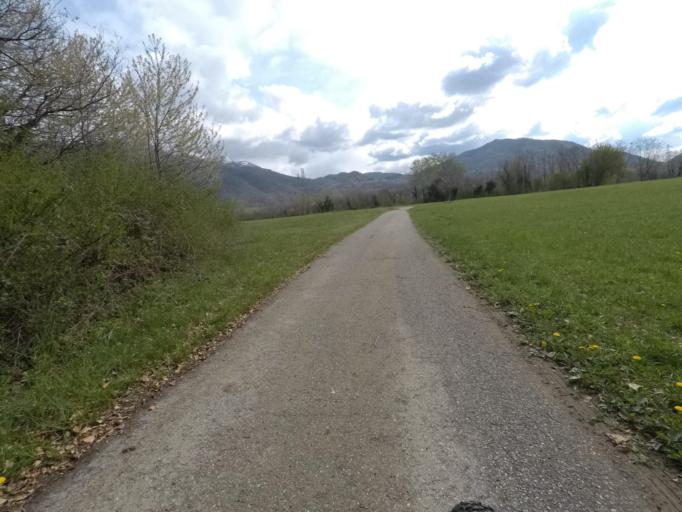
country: IT
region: Friuli Venezia Giulia
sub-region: Provincia di Udine
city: Gemona
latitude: 46.2528
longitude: 13.1312
